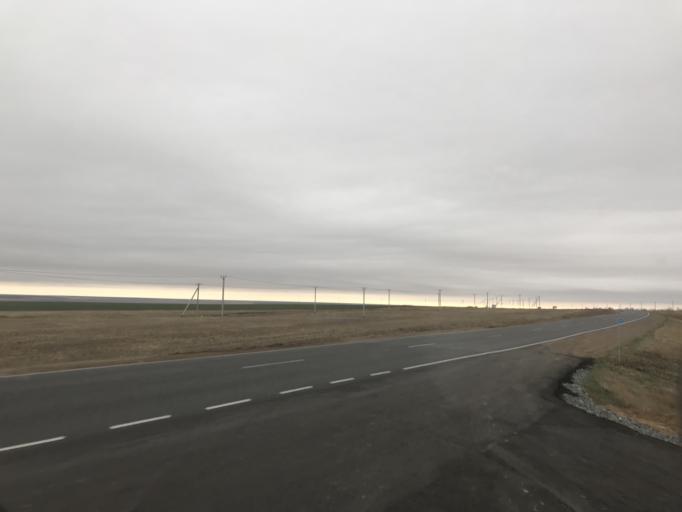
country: KZ
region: Batys Qazaqstan
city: Peremetnoe
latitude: 51.6464
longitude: 51.0125
